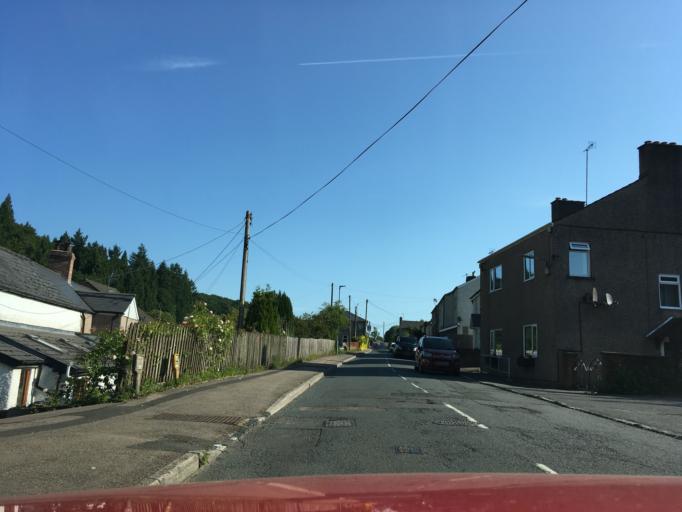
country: GB
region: England
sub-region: Gloucestershire
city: Cinderford
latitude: 51.8006
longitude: -2.5096
